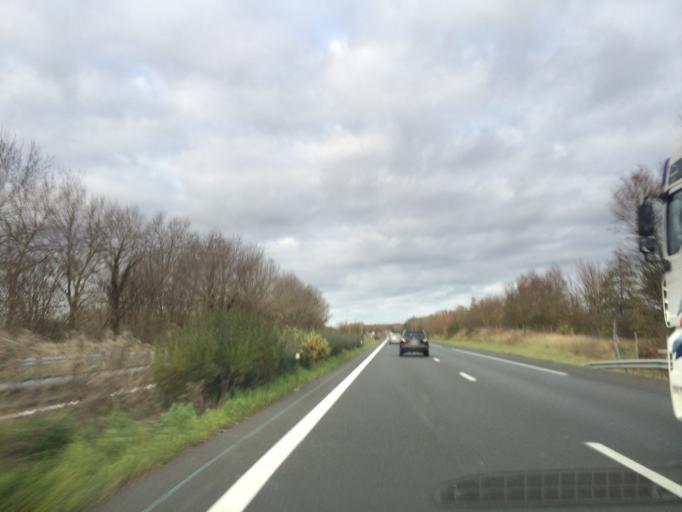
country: FR
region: Poitou-Charentes
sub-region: Departement de la Charente-Maritime
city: Saint-Jean-d'Angely
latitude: 46.0695
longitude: -0.5331
